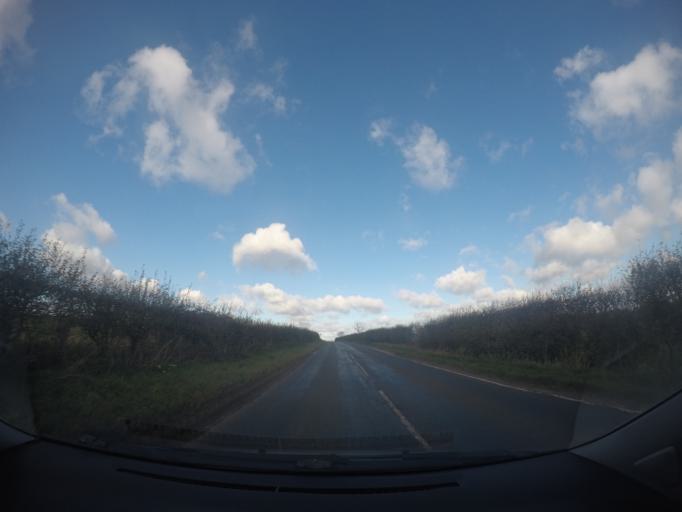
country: GB
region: England
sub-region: City and Borough of Leeds
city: Walton
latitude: 54.0125
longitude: -1.3092
